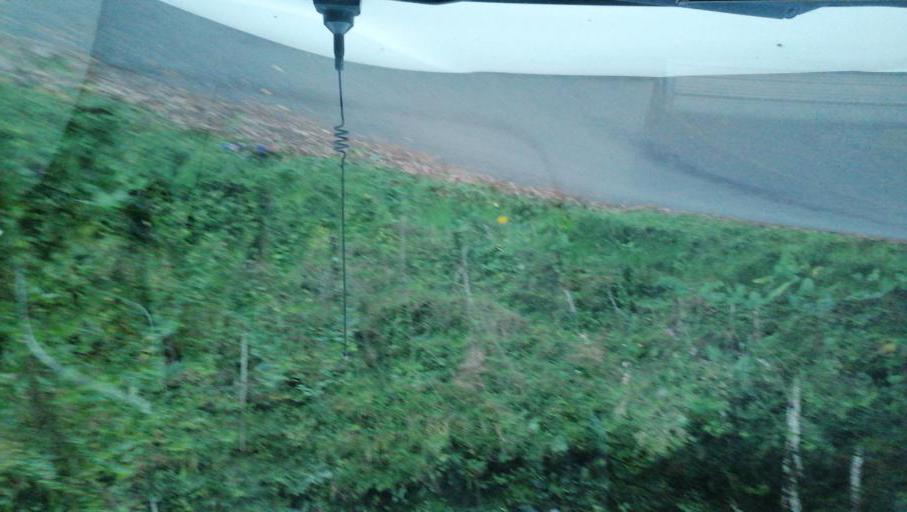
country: MX
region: Chiapas
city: Ostuacan
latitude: 17.4241
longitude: -93.3447
